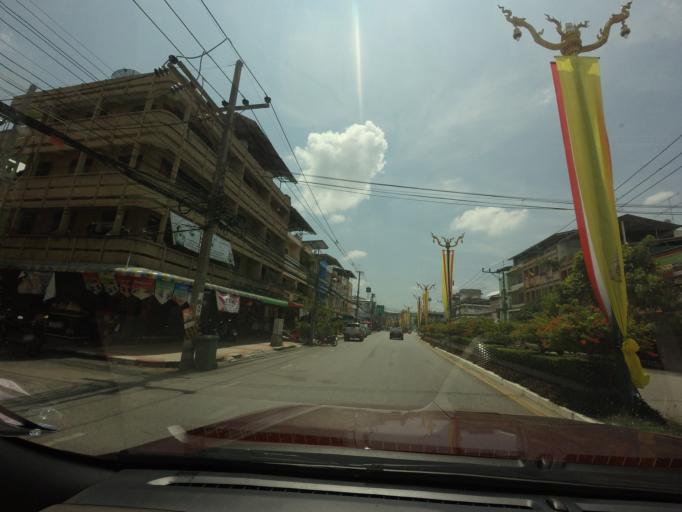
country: TH
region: Yala
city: Betong
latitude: 5.7750
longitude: 101.0722
